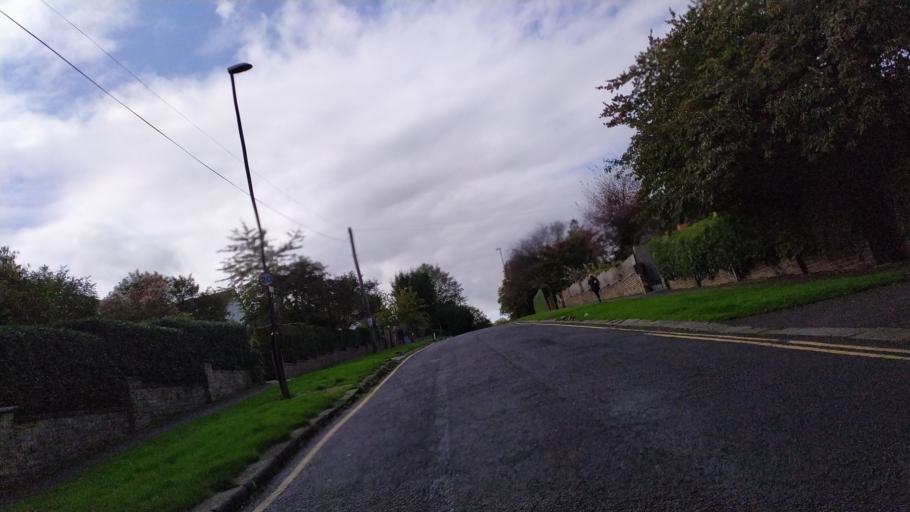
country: GB
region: England
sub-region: City and Borough of Leeds
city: Chapel Allerton
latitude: 53.8316
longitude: -1.5803
